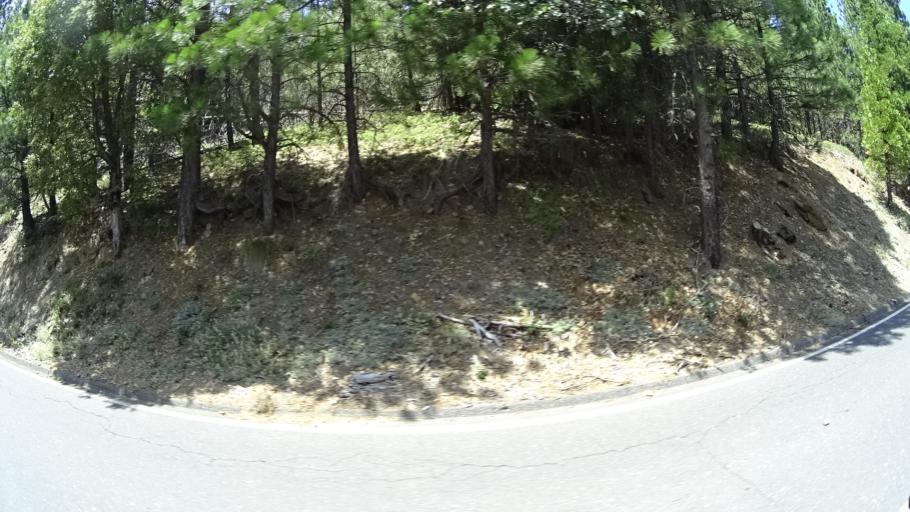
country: US
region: California
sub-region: Calaveras County
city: Arnold
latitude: 38.3090
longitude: -120.2407
